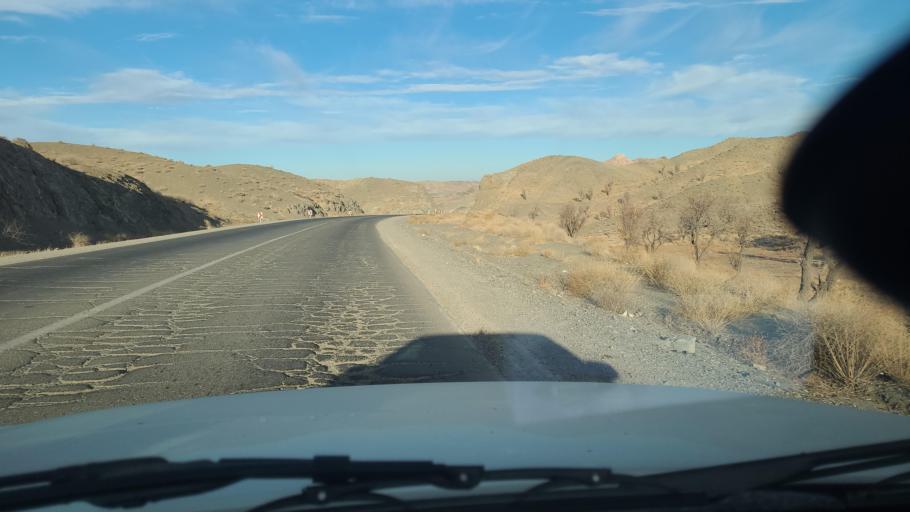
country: IR
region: Razavi Khorasan
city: Sabzevar
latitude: 36.4160
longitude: 57.5524
